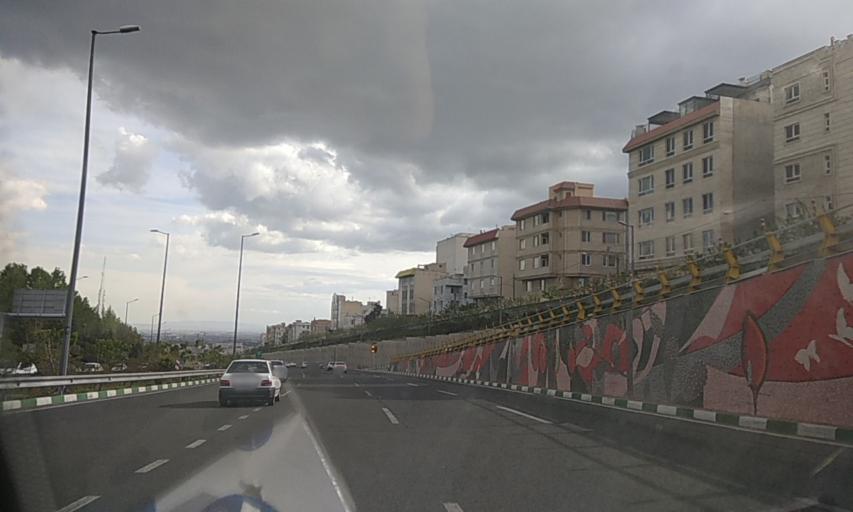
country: IR
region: Tehran
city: Tajrish
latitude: 35.7622
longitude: 51.2960
